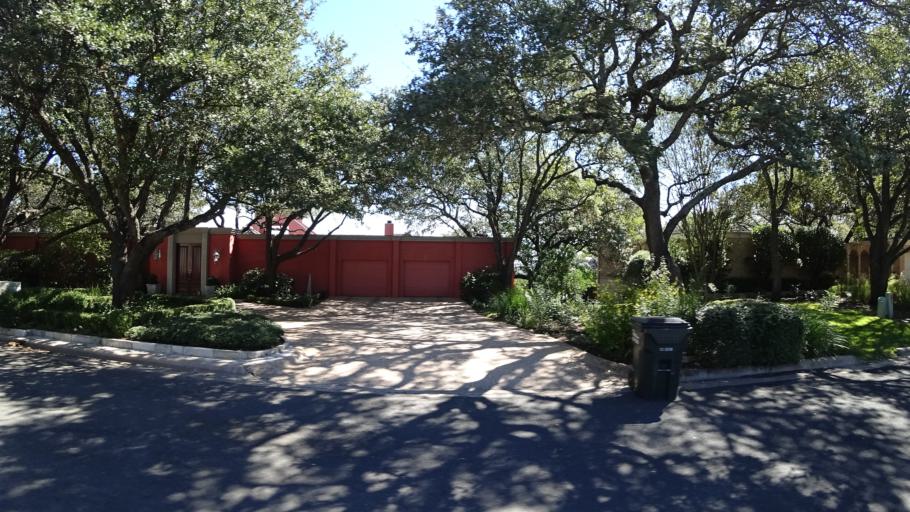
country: US
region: Texas
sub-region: Travis County
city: West Lake Hills
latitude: 30.3129
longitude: -97.7930
